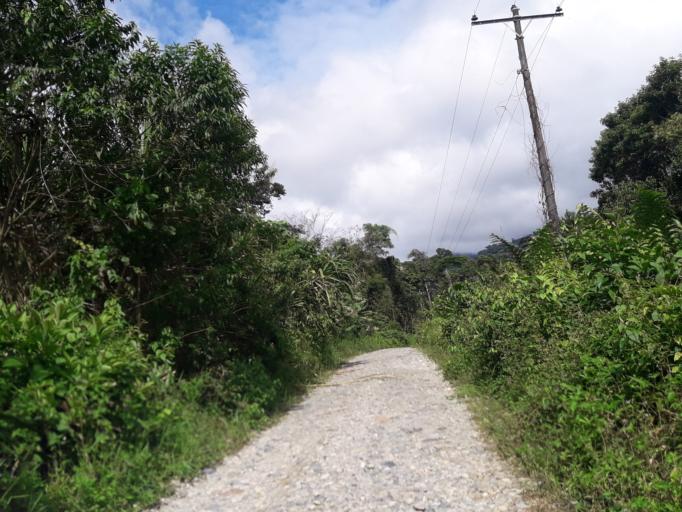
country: EC
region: Napo
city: Archidona
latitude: -0.9425
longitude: -77.8828
